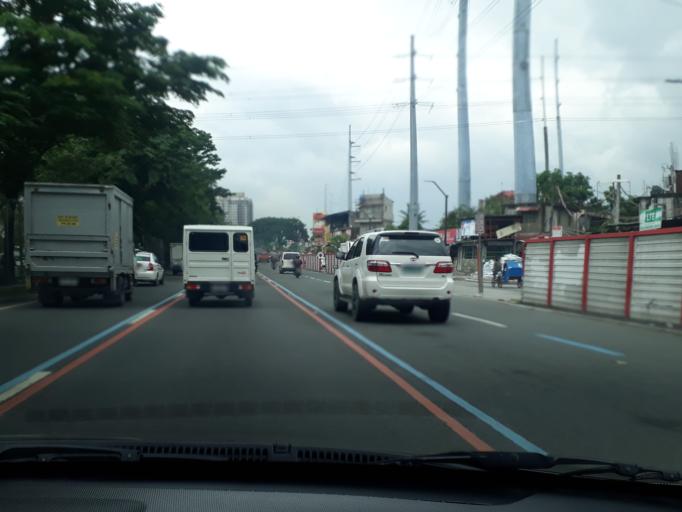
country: PH
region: Calabarzon
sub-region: Province of Rizal
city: Pateros
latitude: 14.5359
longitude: 121.0575
